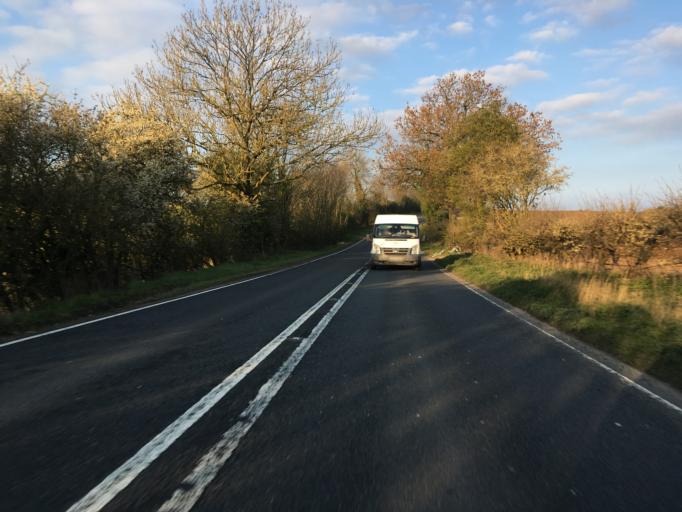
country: GB
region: England
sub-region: Gloucestershire
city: Charlton Kings
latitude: 51.8482
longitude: -2.0563
